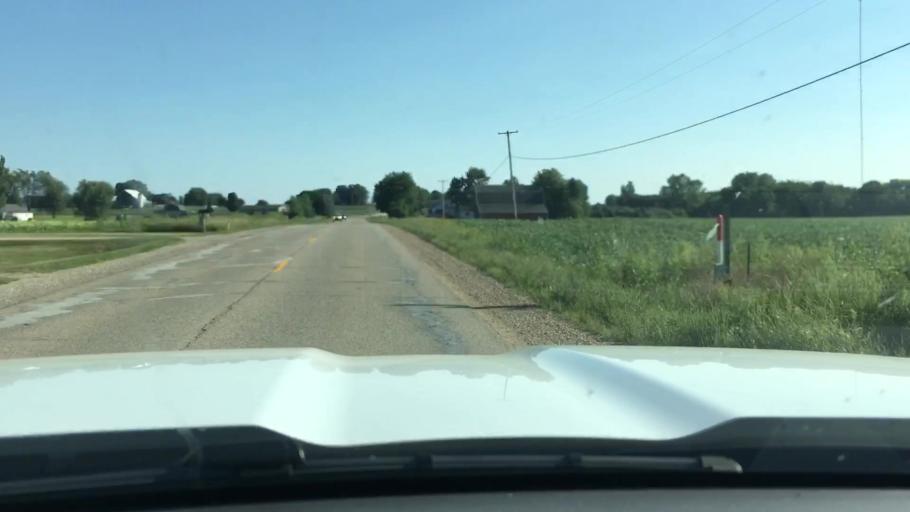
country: US
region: Michigan
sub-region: Ottawa County
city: Zeeland
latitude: 42.8601
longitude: -85.9600
